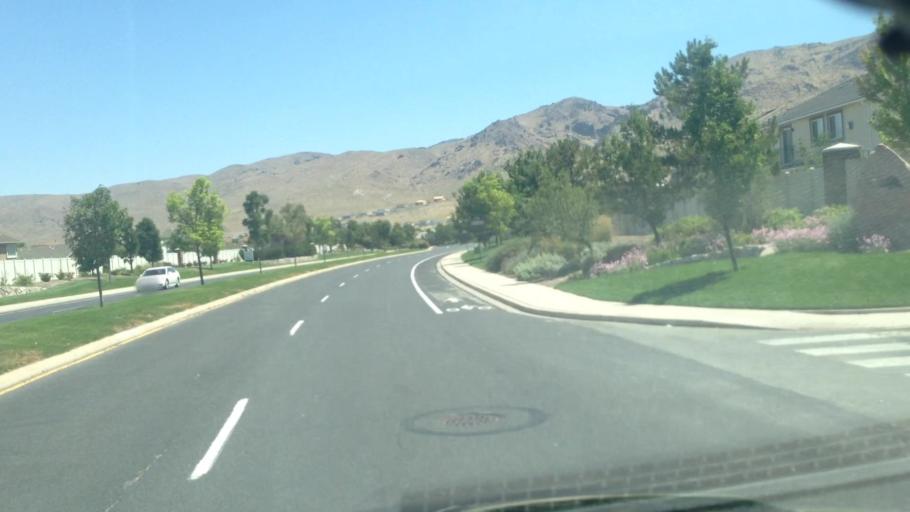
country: US
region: Nevada
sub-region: Washoe County
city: Sparks
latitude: 39.4173
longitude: -119.7225
